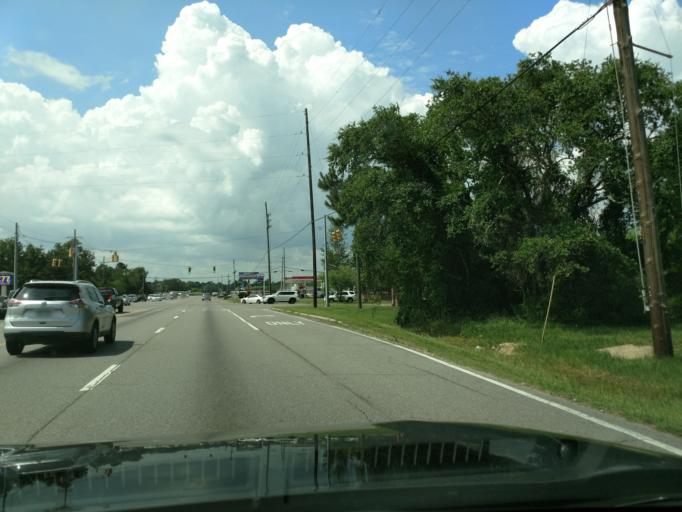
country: US
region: Mississippi
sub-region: Jackson County
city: Gulf Hills
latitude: 30.4314
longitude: -88.8296
